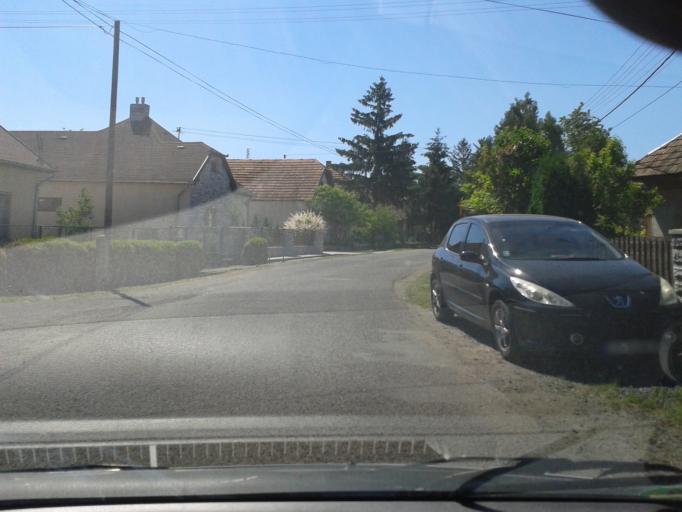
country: SK
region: Nitriansky
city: Levice
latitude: 48.1690
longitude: 18.5511
